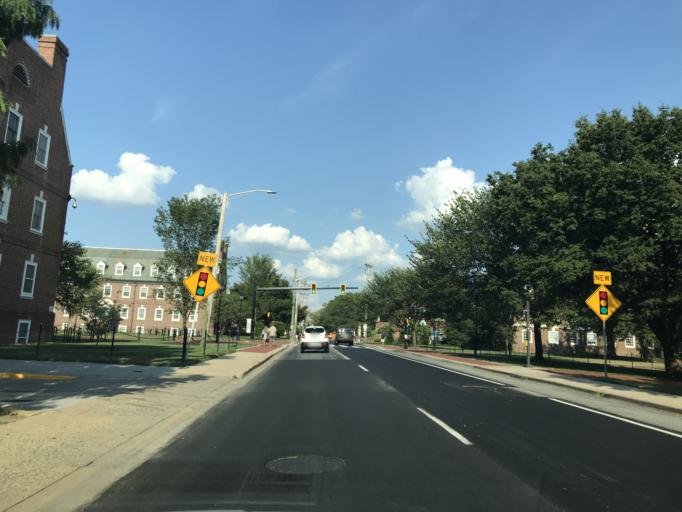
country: US
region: Delaware
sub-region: New Castle County
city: Newark
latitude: 39.6817
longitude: -75.7532
